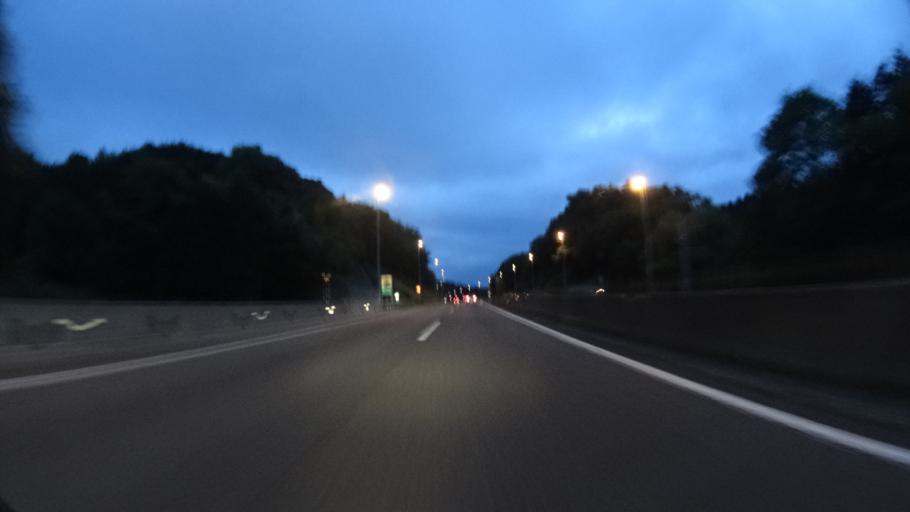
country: JP
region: Shiga Prefecture
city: Hikone
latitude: 35.1812
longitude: 136.2820
